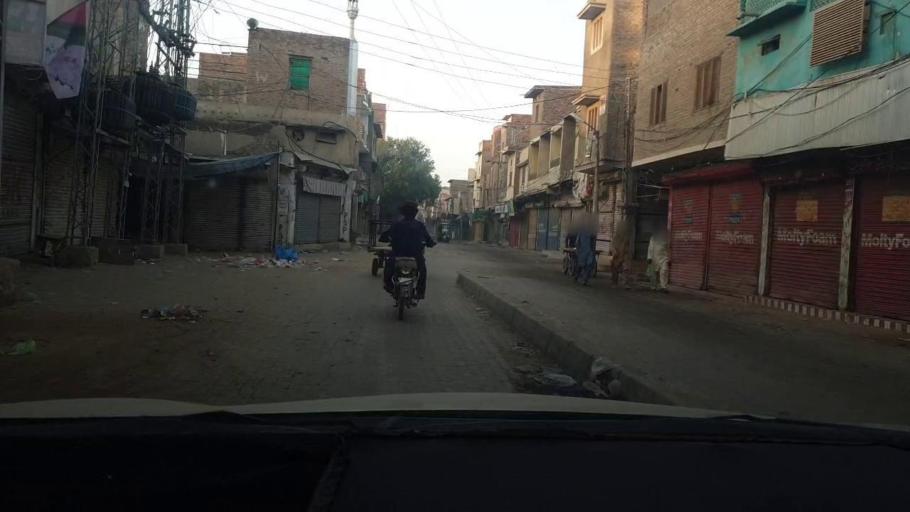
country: PK
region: Sindh
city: Larkana
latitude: 27.5570
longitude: 68.2162
